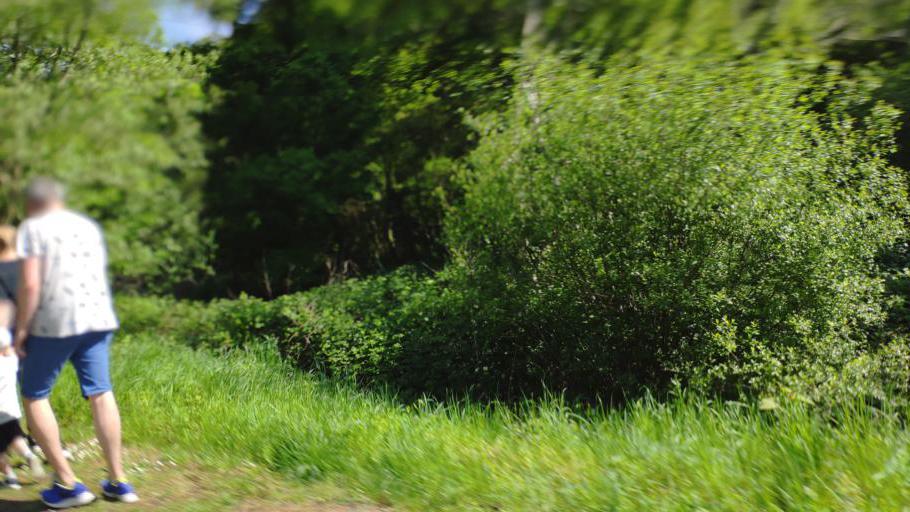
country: IE
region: Munster
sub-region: County Cork
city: Blarney
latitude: 51.9435
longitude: -8.5657
